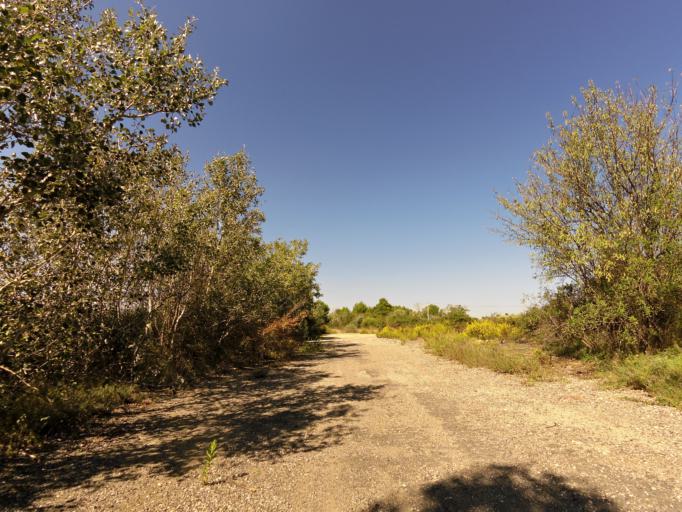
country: FR
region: Languedoc-Roussillon
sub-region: Departement de l'Herault
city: Villetelle
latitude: 43.7253
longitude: 4.1512
